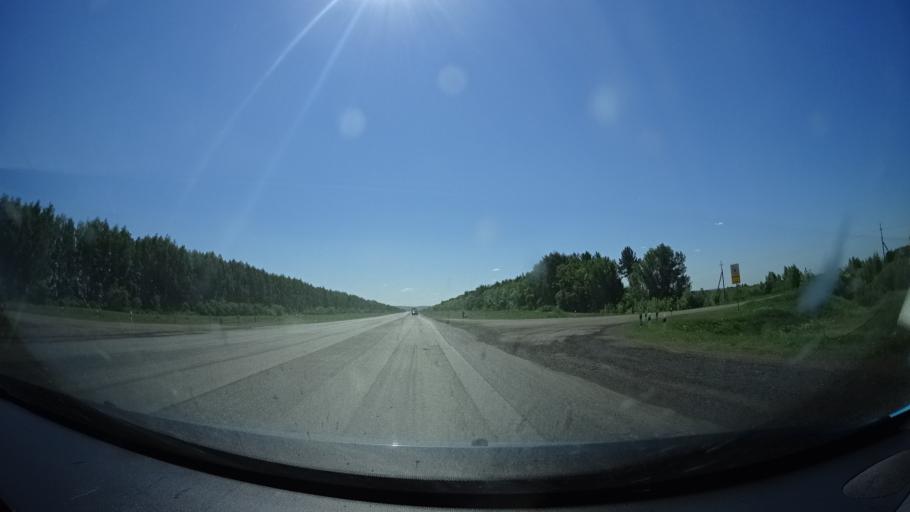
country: RU
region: Bashkortostan
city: Birsk
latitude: 55.2409
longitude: 55.7689
